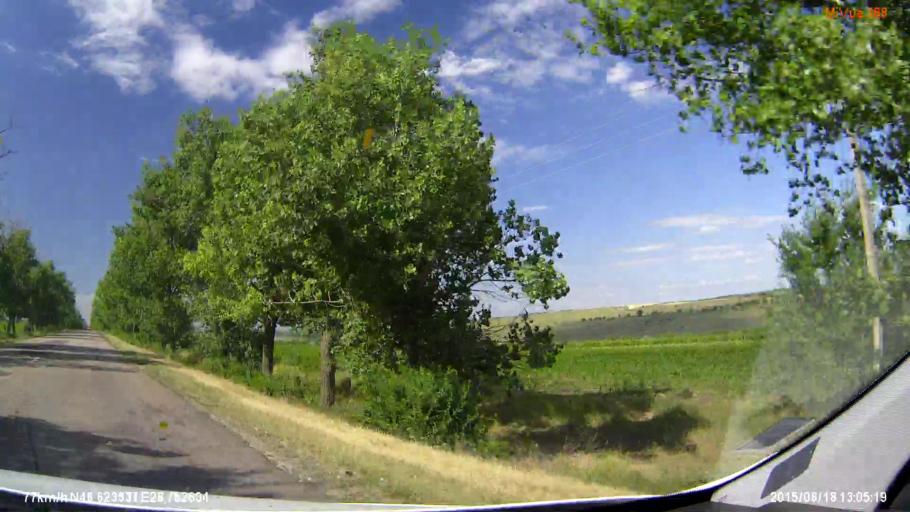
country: MD
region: Cimislia
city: Cimislia
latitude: 46.6233
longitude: 28.7526
